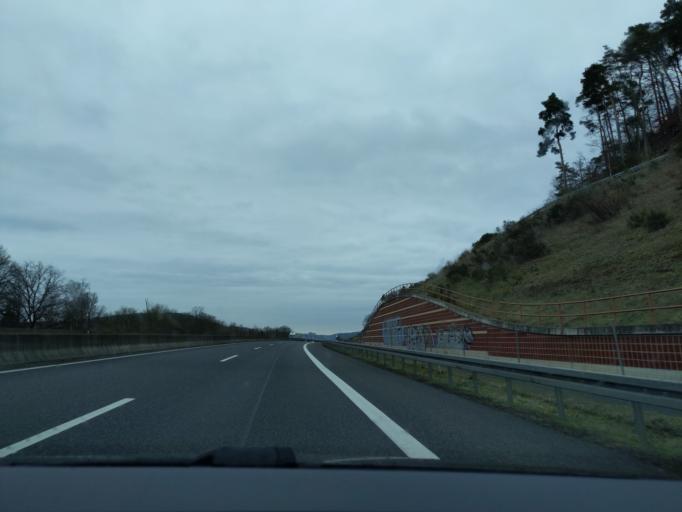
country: DE
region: Hesse
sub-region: Regierungsbezirk Giessen
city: Fronhausen
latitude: 50.7400
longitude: 8.7380
